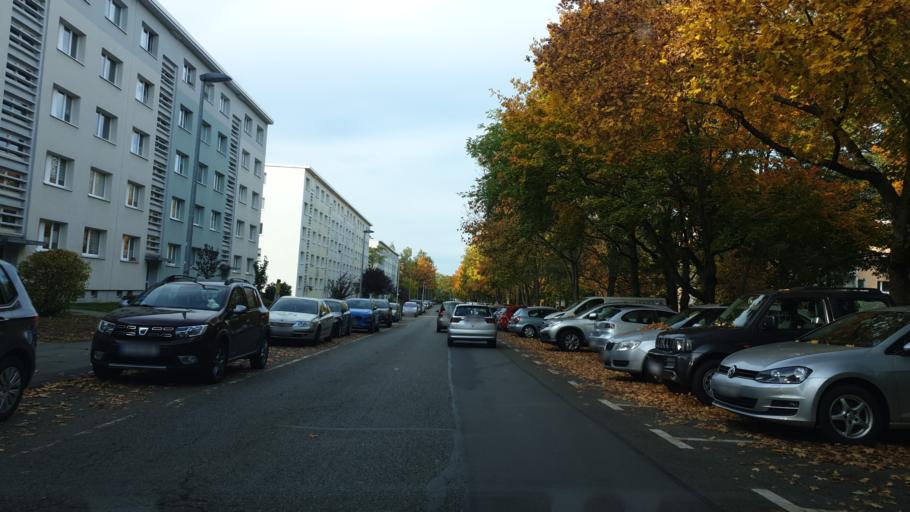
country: DE
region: Saxony
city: Hilbersdorf
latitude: 50.8246
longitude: 12.9584
